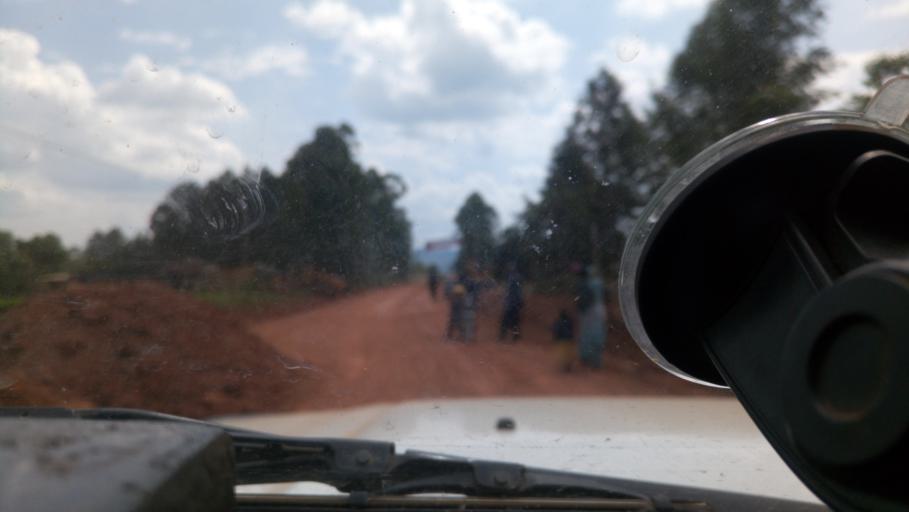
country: KE
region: Kericho
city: Litein
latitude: -0.5811
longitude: 35.1172
